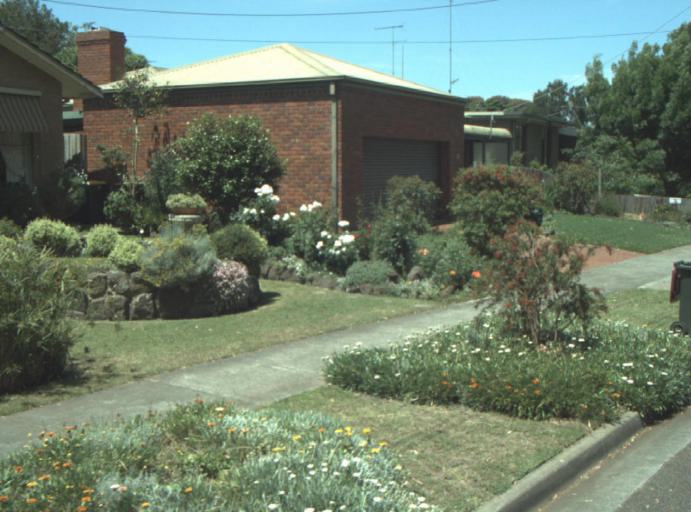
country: AU
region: Victoria
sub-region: Greater Geelong
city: Wandana Heights
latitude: -38.1591
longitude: 144.3233
